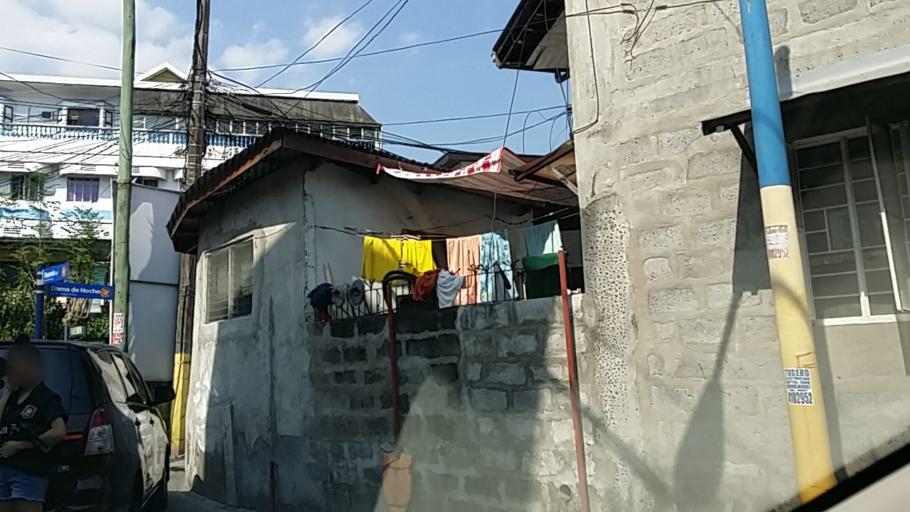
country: PH
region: Metro Manila
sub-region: Mandaluyong
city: Mandaluyong City
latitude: 14.5732
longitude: 121.0359
